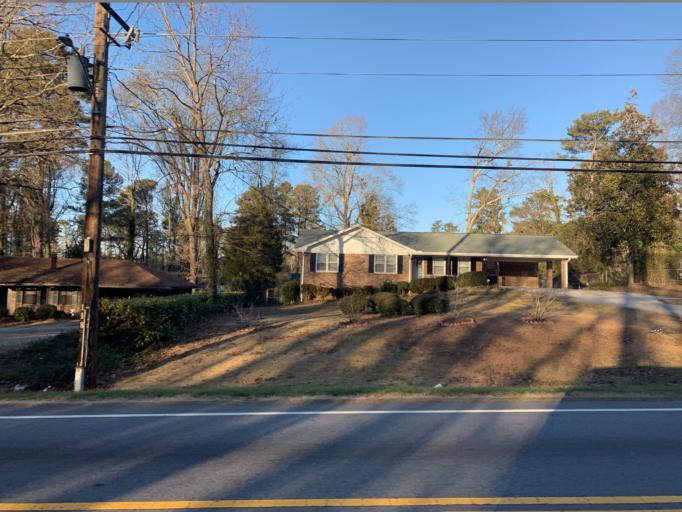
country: US
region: Georgia
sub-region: Gwinnett County
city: Lilburn
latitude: 33.8772
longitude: -84.1096
